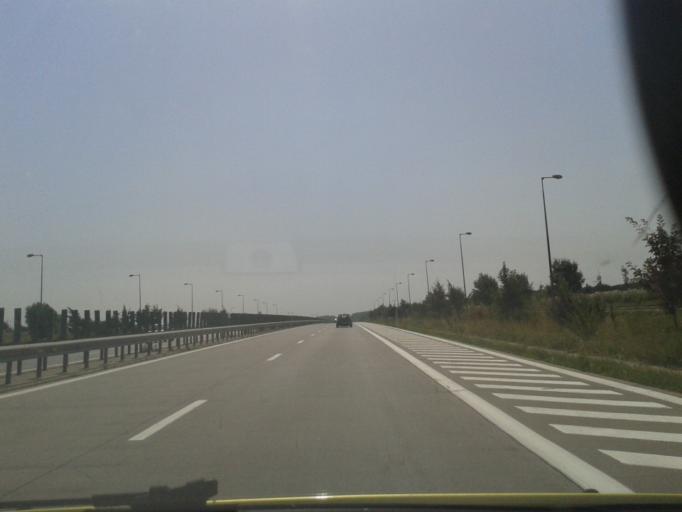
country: RO
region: Ilfov
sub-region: Comuna Cernica
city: Tanganu
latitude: 44.4231
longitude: 26.3311
